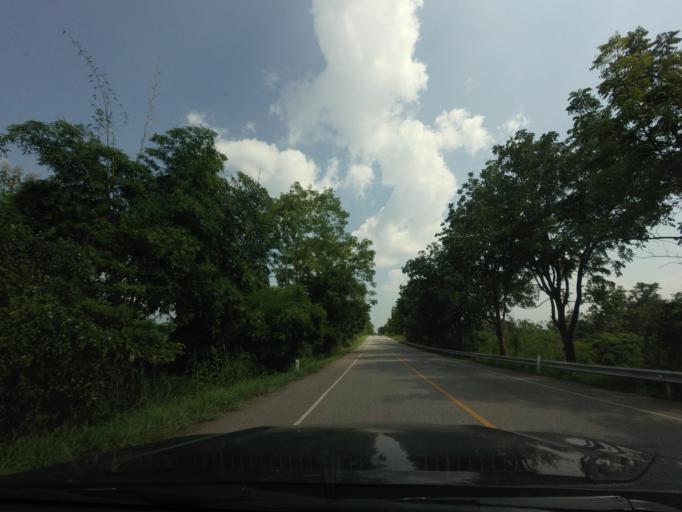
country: TH
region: Phitsanulok
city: Chat Trakan
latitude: 17.2670
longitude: 100.5492
